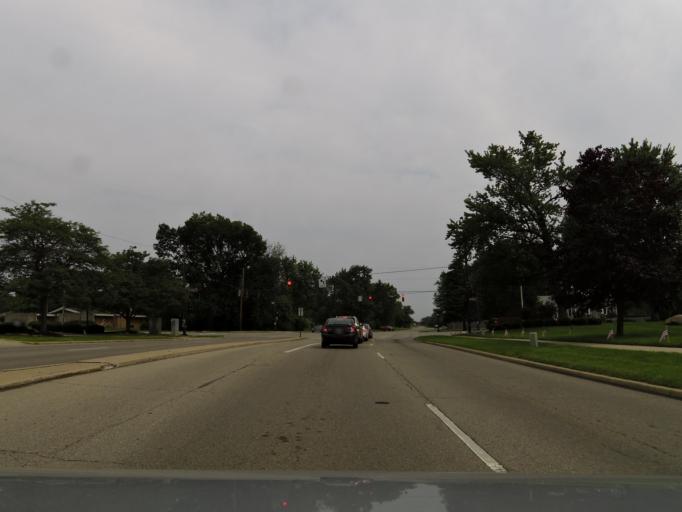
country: US
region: Ohio
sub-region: Montgomery County
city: Kettering
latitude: 39.6881
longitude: -84.1279
